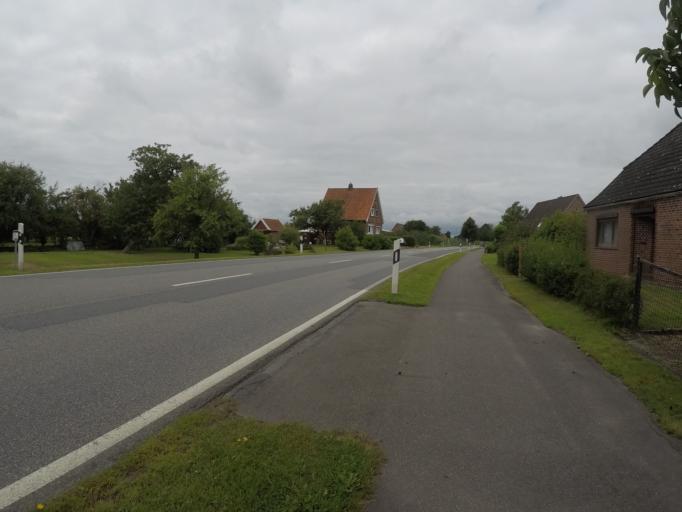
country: DE
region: Lower Saxony
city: Mittelnkirchen
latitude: 53.5391
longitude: 9.6274
